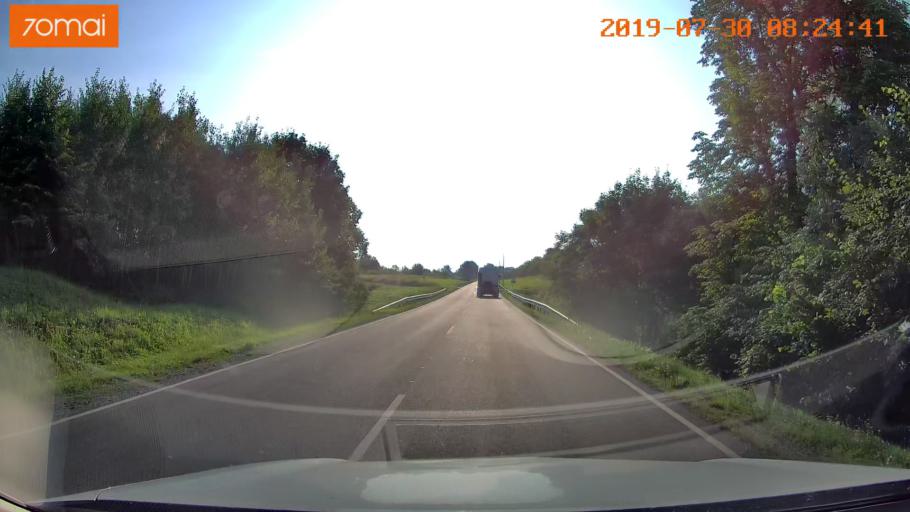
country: RU
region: Kaliningrad
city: Chernyakhovsk
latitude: 54.6236
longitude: 21.5626
